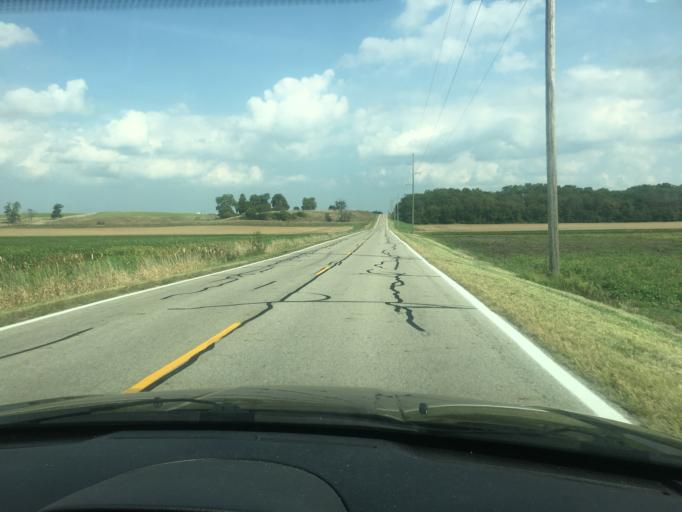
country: US
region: Ohio
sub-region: Champaign County
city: Urbana
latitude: 40.1288
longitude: -83.7903
